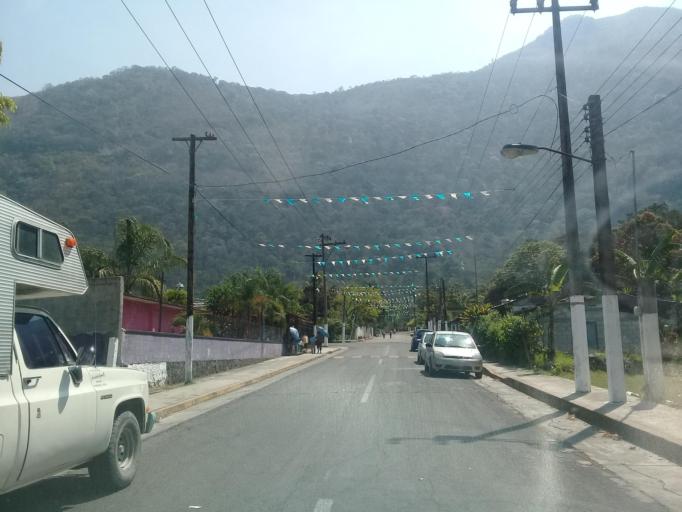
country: MX
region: Veracruz
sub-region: Ixtaczoquitlan
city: Capoluca
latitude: 18.8048
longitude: -96.9876
